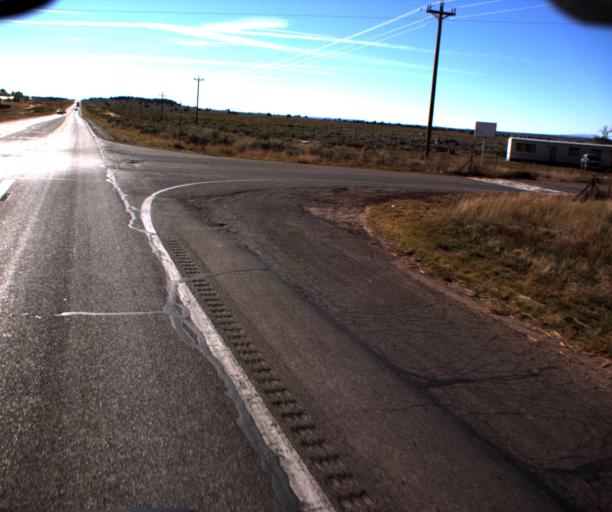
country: US
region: Arizona
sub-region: Mohave County
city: Colorado City
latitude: 36.9835
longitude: -112.9855
